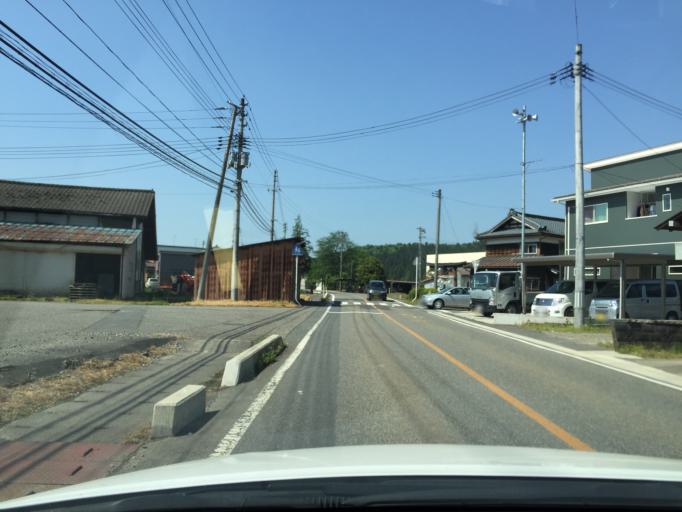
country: JP
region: Niigata
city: Muramatsu
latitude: 37.6827
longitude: 139.1514
